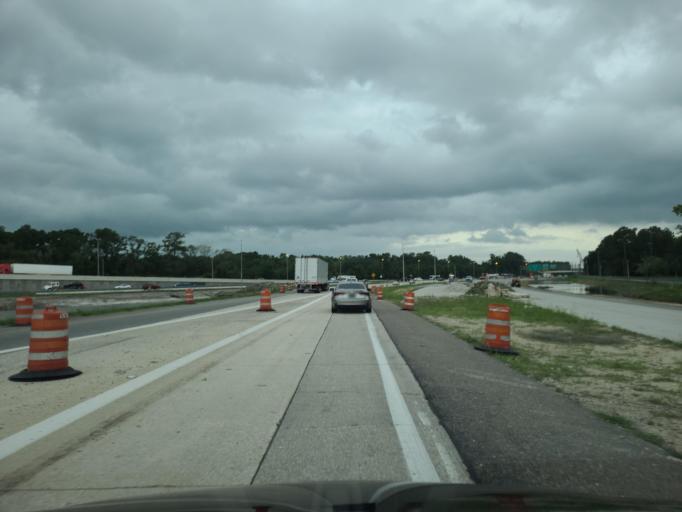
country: US
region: Florida
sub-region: Duval County
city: Jacksonville
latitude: 30.4629
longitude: -81.6470
